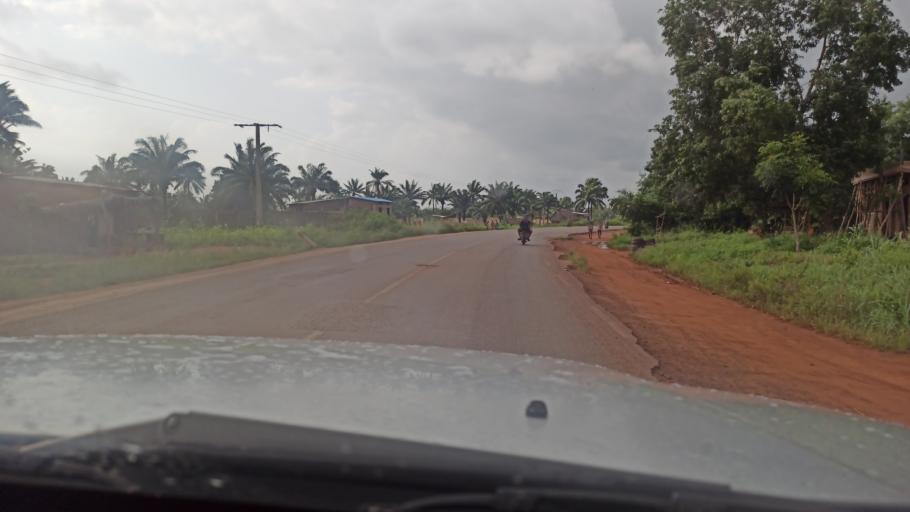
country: BJ
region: Queme
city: Porto-Novo
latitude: 6.5701
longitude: 2.5768
